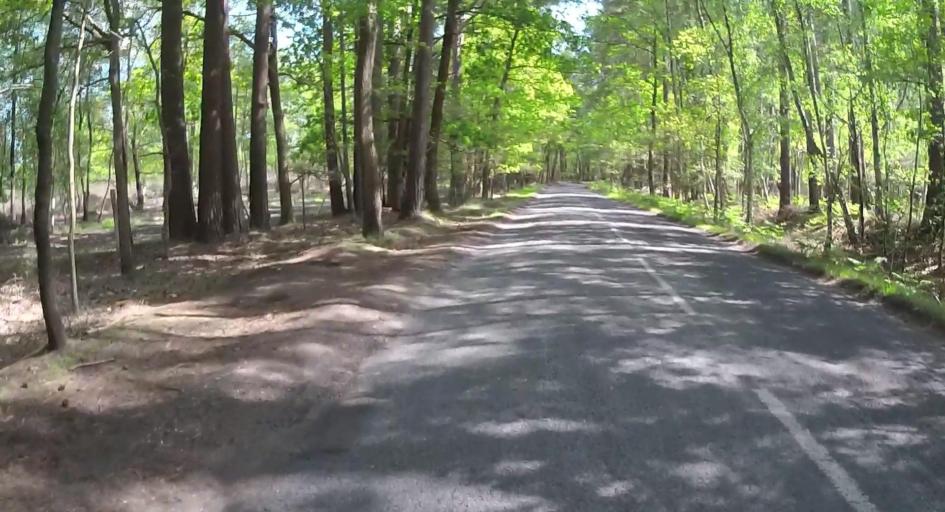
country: GB
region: England
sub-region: Surrey
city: Farnham
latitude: 51.1829
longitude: -0.7804
